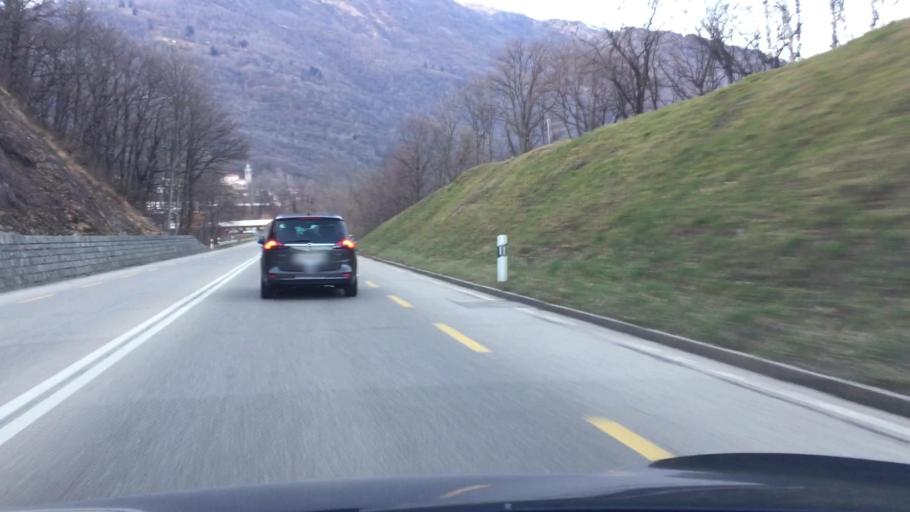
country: CH
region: Ticino
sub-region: Lugano District
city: Gravesano
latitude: 46.0764
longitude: 8.9234
